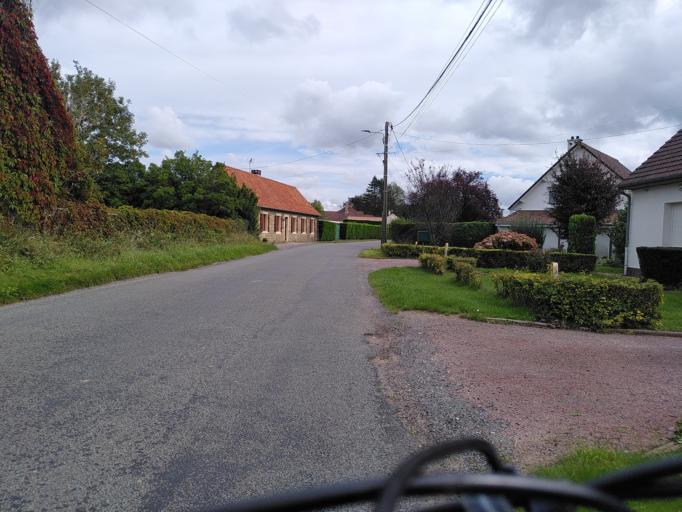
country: FR
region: Nord-Pas-de-Calais
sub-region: Departement du Pas-de-Calais
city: La Capelle-les-Boulogne
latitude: 50.7113
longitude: 1.7522
